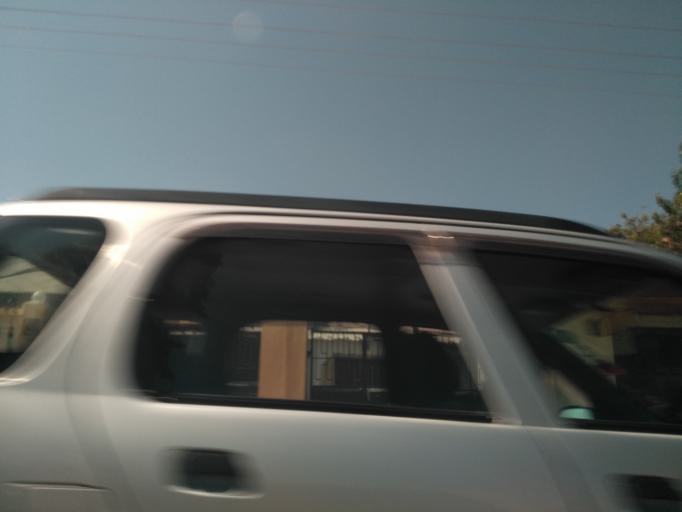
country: TZ
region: Dodoma
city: Dodoma
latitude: -6.1673
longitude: 35.7483
